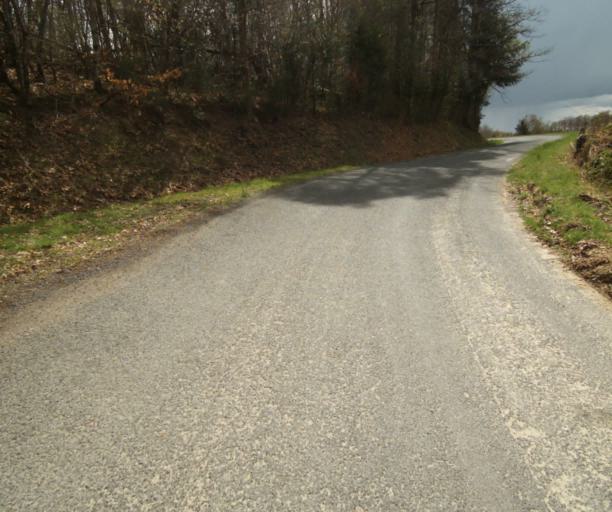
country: FR
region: Limousin
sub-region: Departement de la Correze
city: Laguenne
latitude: 45.2538
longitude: 1.8784
